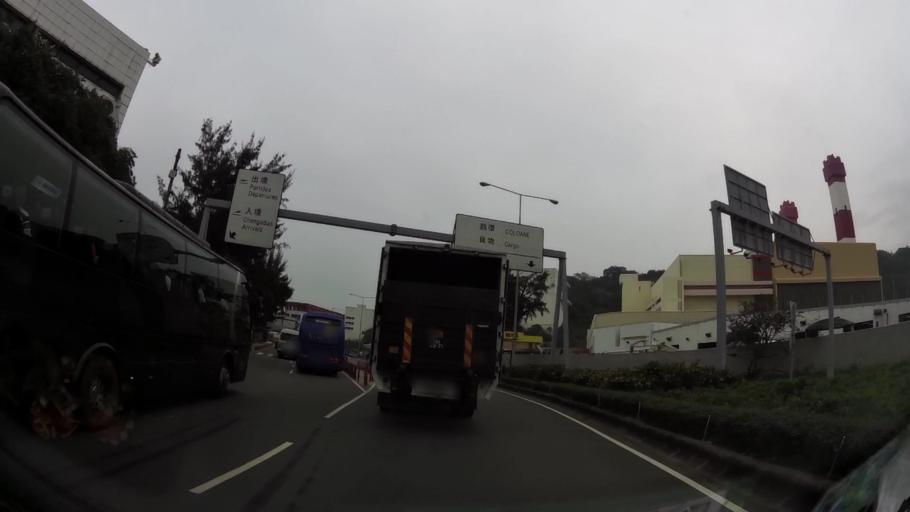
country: MO
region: Macau
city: Macau
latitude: 22.1623
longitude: 113.5736
